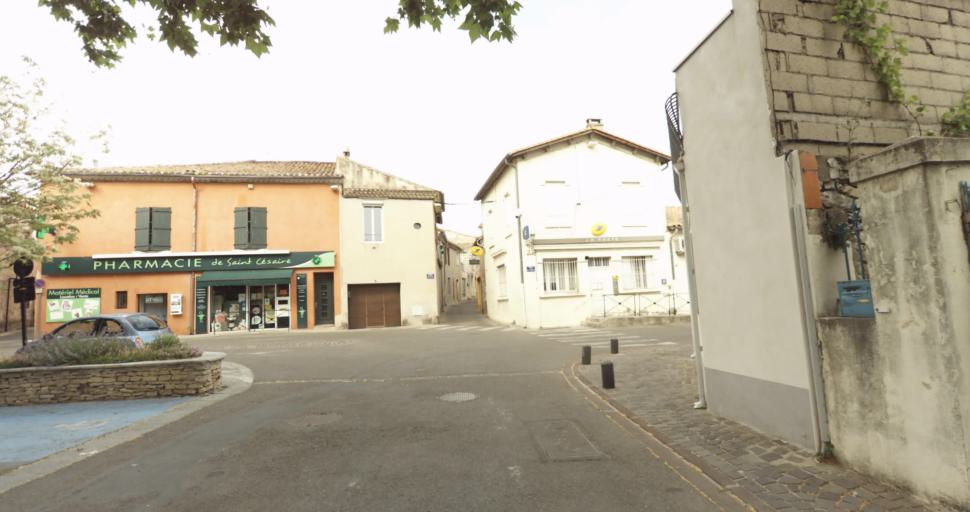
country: FR
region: Languedoc-Roussillon
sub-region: Departement du Gard
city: Nimes
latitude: 43.8161
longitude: 4.3270
